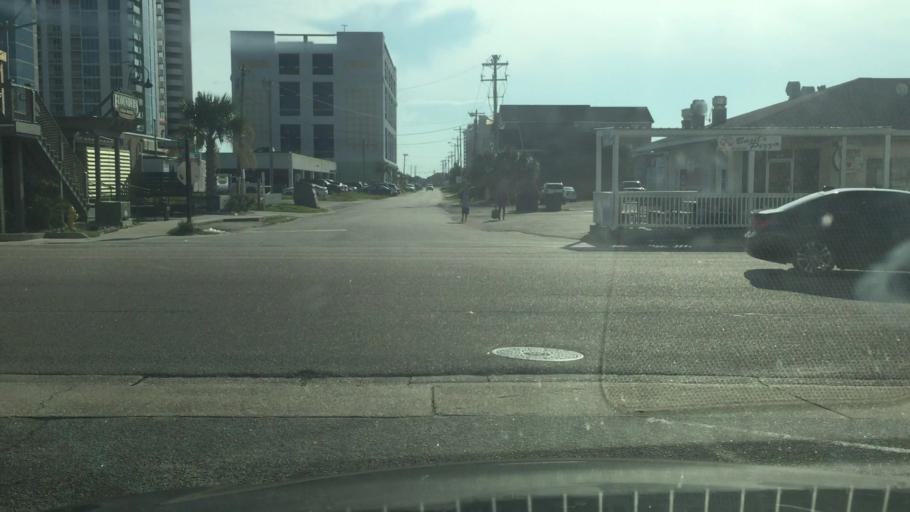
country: US
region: South Carolina
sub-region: Horry County
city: North Myrtle Beach
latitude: 33.8284
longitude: -78.6430
